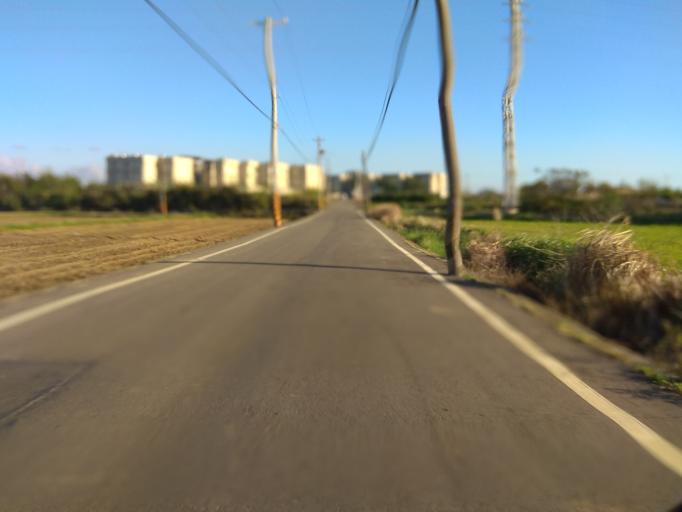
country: TW
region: Taiwan
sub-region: Hsinchu
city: Zhubei
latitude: 24.9901
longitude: 121.0514
